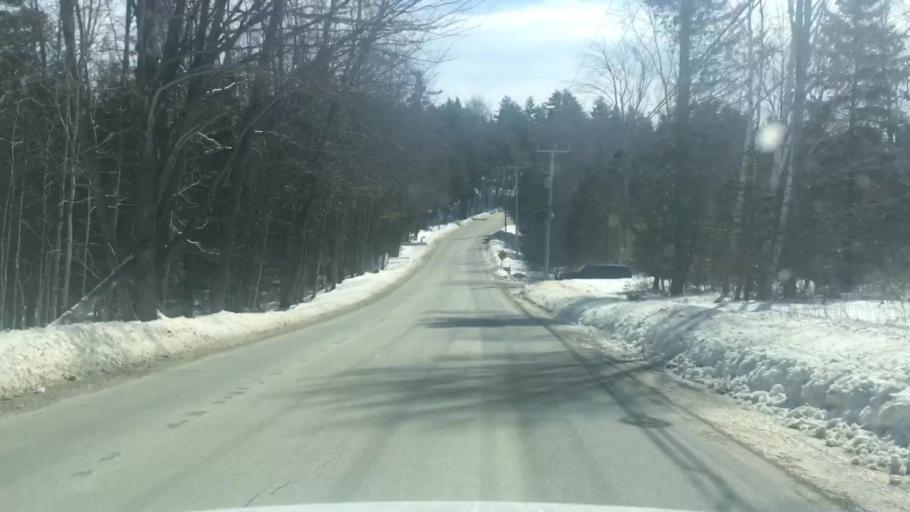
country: US
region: Maine
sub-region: Penobscot County
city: Holden
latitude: 44.7518
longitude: -68.6333
